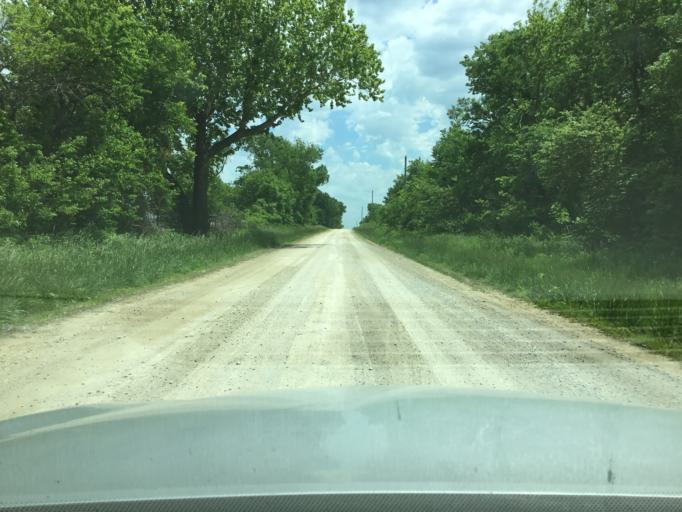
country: US
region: Kansas
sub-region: Montgomery County
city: Caney
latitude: 37.0953
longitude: -95.8192
